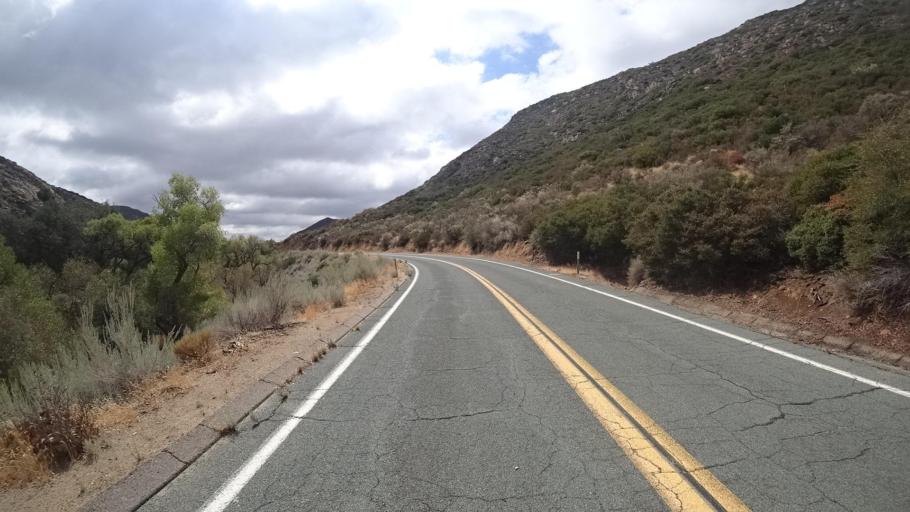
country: US
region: California
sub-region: San Diego County
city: Pine Valley
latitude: 32.7745
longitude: -116.4503
